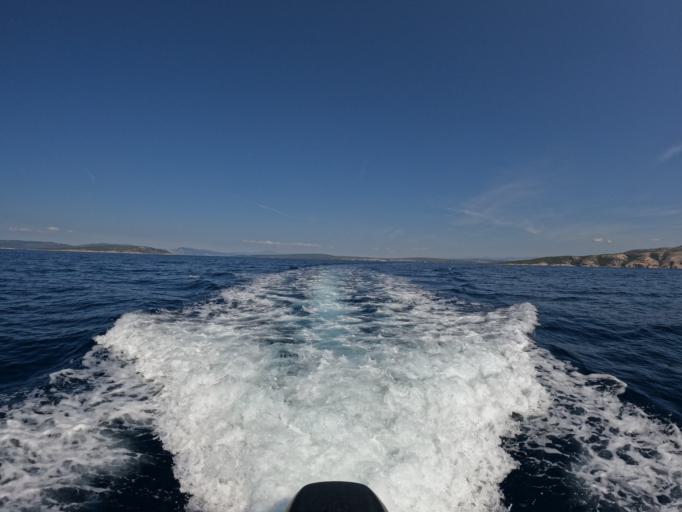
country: HR
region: Primorsko-Goranska
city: Punat
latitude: 44.9470
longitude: 14.6137
